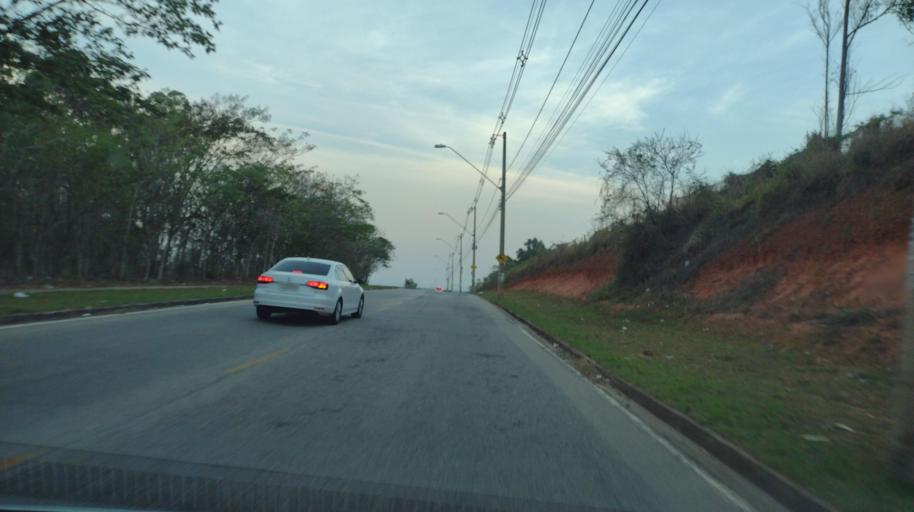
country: BR
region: Sao Paulo
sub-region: Sorocaba
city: Sorocaba
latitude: -23.3785
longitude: -47.4744
